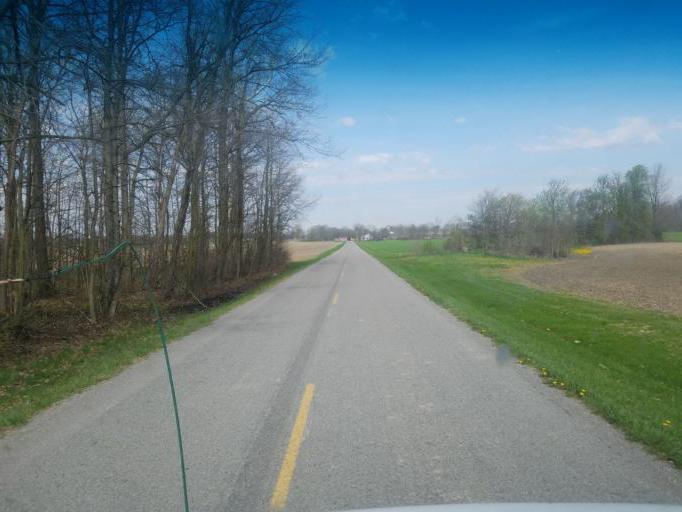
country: US
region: Ohio
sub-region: Logan County
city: Northwood
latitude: 40.4939
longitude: -83.6248
